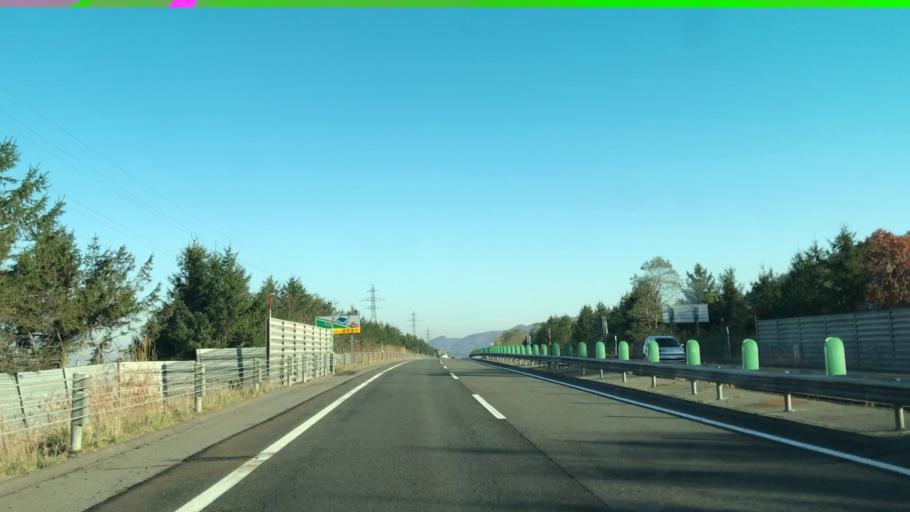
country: JP
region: Hokkaido
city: Sunagawa
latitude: 43.4236
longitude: 141.9116
